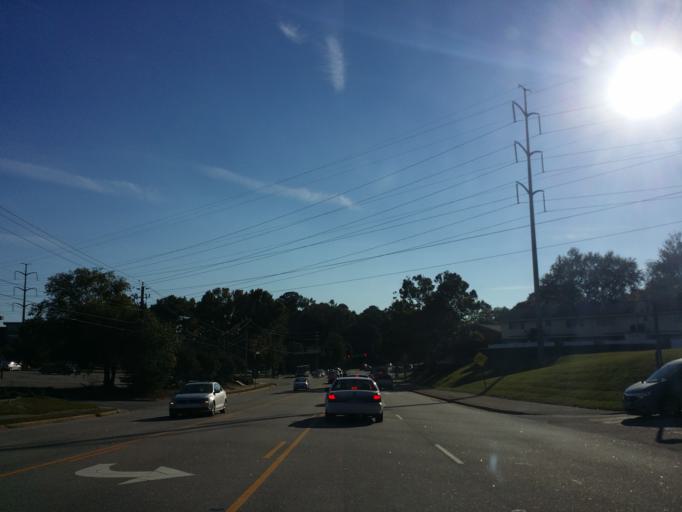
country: US
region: North Carolina
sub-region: Wake County
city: West Raleigh
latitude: 35.7781
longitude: -78.6777
